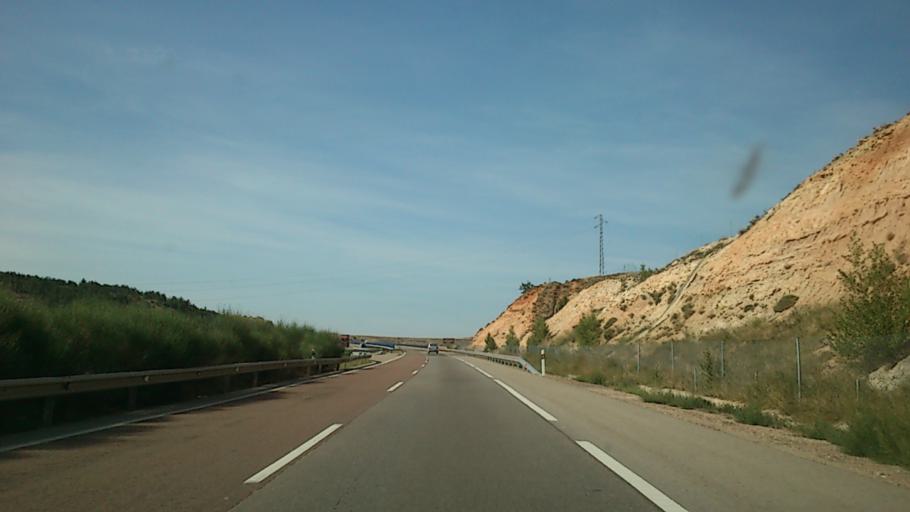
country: ES
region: Aragon
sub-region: Provincia de Teruel
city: Calamocha
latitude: 40.9885
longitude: -1.2594
